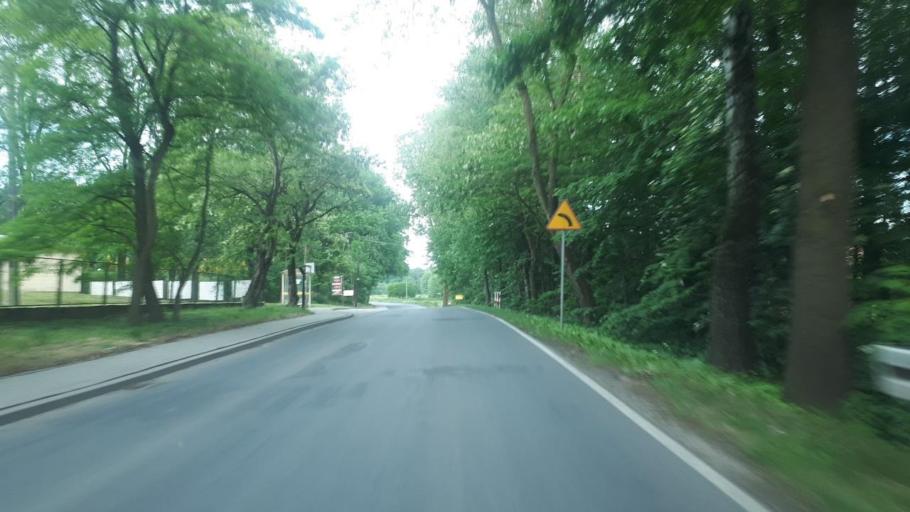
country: PL
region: Silesian Voivodeship
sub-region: Powiat bielski
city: Pisarzowice
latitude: 49.9027
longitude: 19.1231
